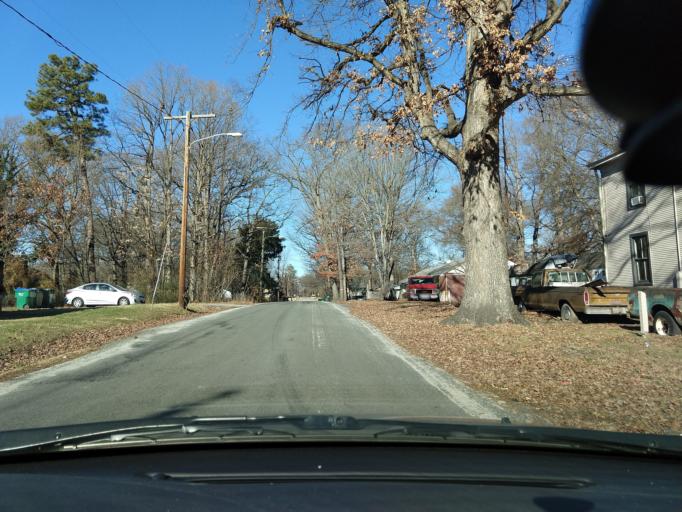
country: US
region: Virginia
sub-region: Chesterfield County
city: Bensley
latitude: 37.4711
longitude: -77.4407
